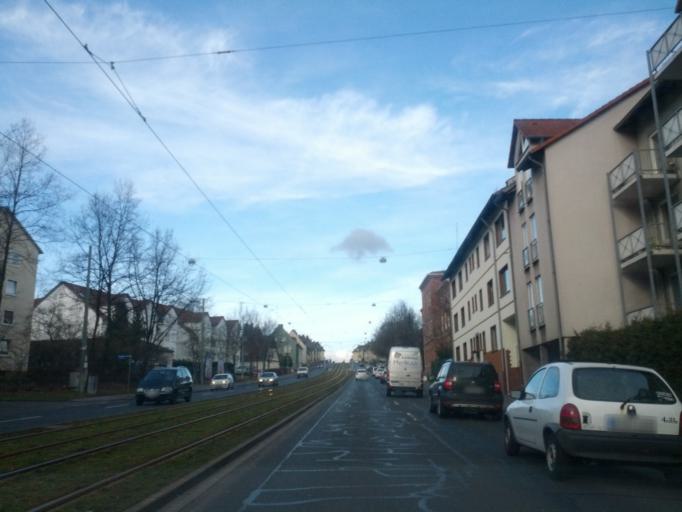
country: DE
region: Hesse
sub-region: Regierungsbezirk Kassel
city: Kassel
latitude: 51.3257
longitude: 9.5132
